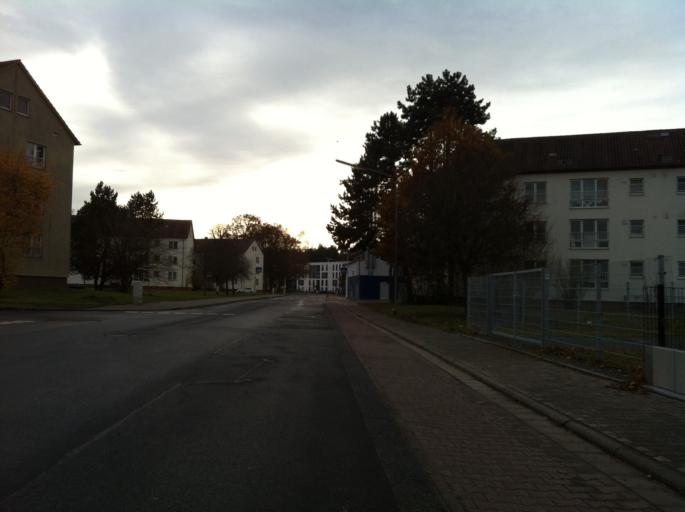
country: DE
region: Hesse
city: Langen
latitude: 50.0029
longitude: 8.6449
